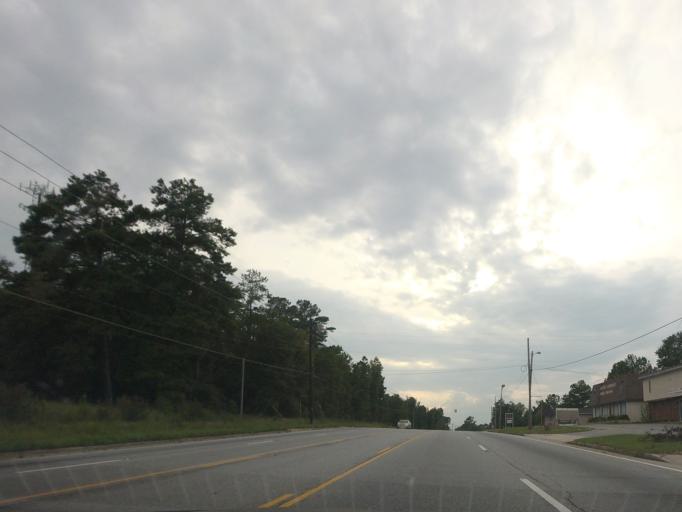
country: US
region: Georgia
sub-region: Bibb County
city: Macon
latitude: 32.8419
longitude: -83.5629
